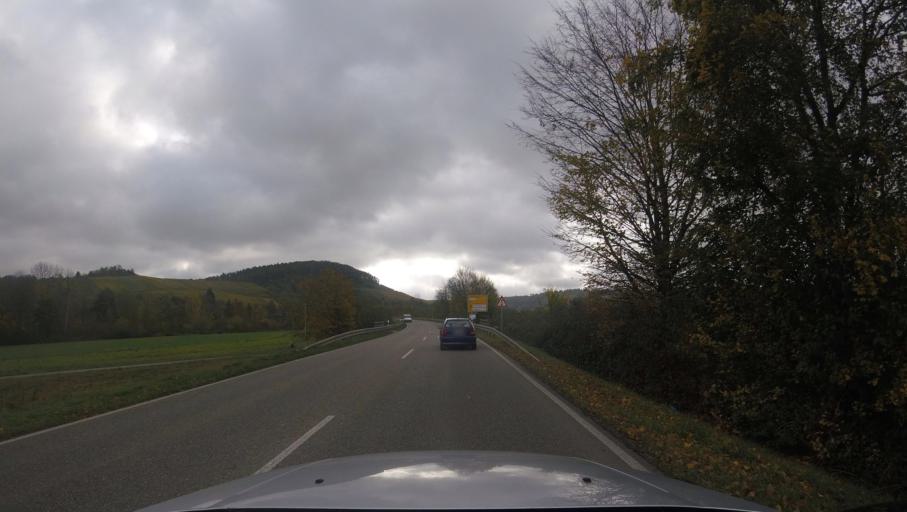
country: DE
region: Baden-Wuerttemberg
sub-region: Regierungsbezirk Stuttgart
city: Winnenden
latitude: 48.8659
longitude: 9.3913
